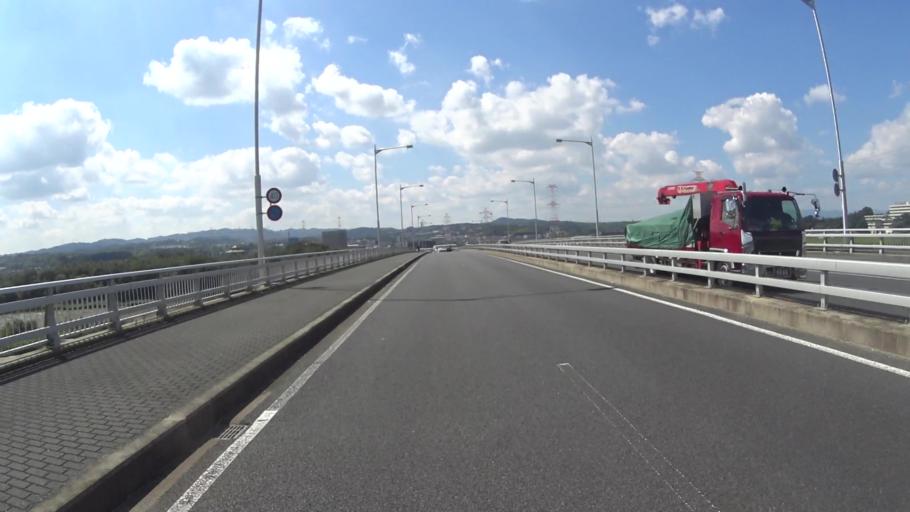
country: JP
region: Kyoto
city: Tanabe
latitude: 34.7989
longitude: 135.7992
